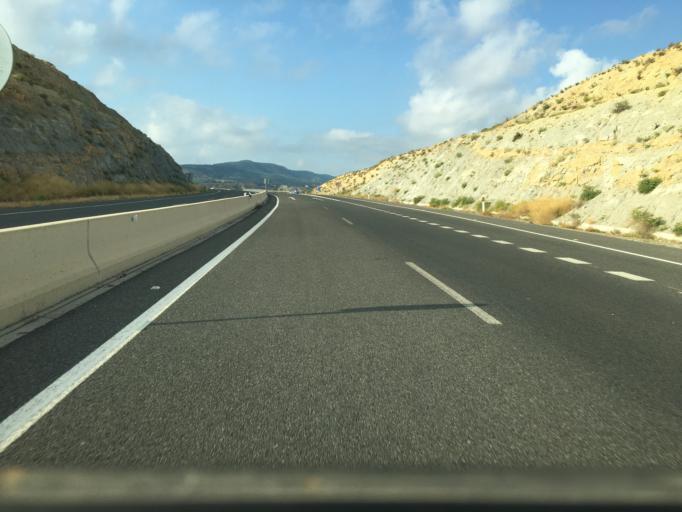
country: ES
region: Murcia
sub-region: Murcia
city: Beniel
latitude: 37.9829
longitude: -0.9746
